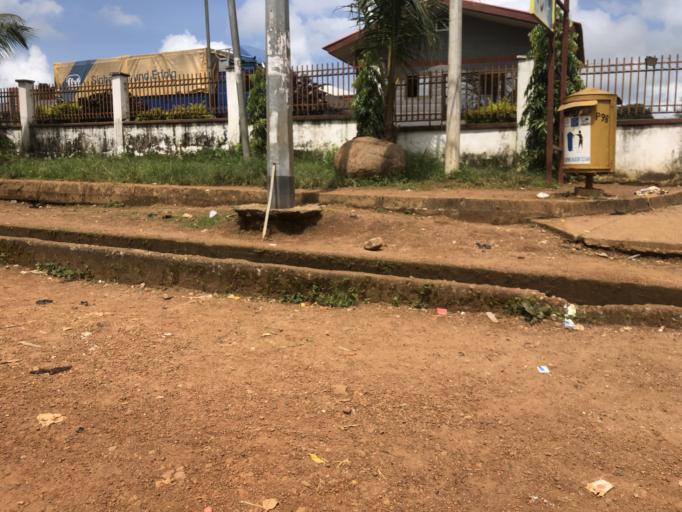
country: SL
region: Northern Province
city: Makeni
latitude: 8.8747
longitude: -12.0518
